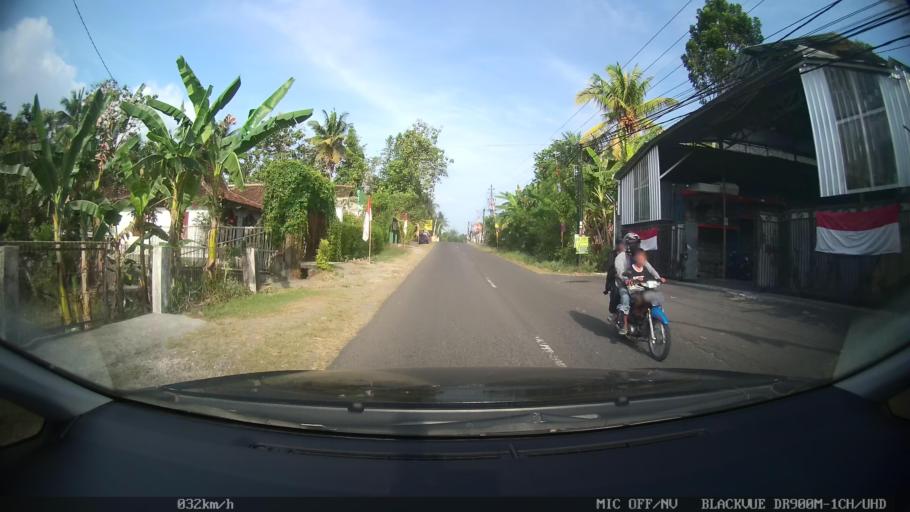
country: ID
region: Daerah Istimewa Yogyakarta
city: Kasihan
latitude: -7.8499
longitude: 110.3157
